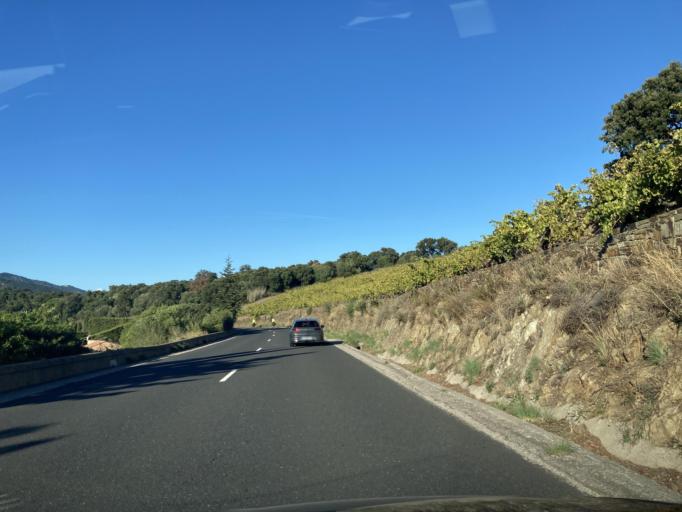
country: FR
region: Languedoc-Roussillon
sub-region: Departement des Pyrenees-Orientales
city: Collioure
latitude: 42.5257
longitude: 3.0720
